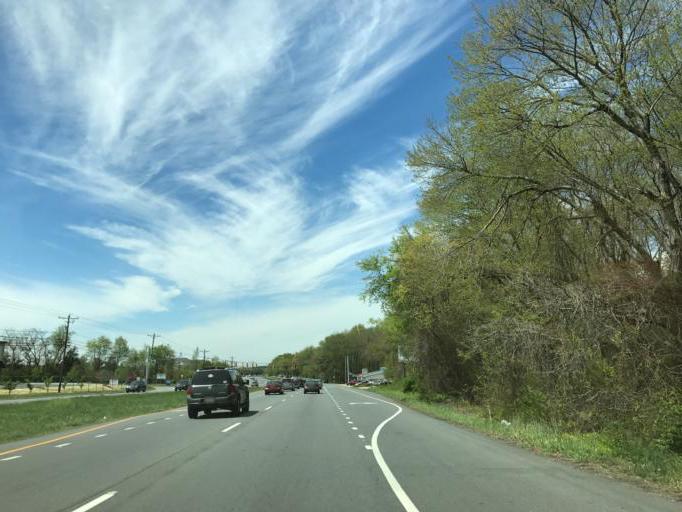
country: US
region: Delaware
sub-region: New Castle County
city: Glasgow
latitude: 39.6047
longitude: -75.7674
